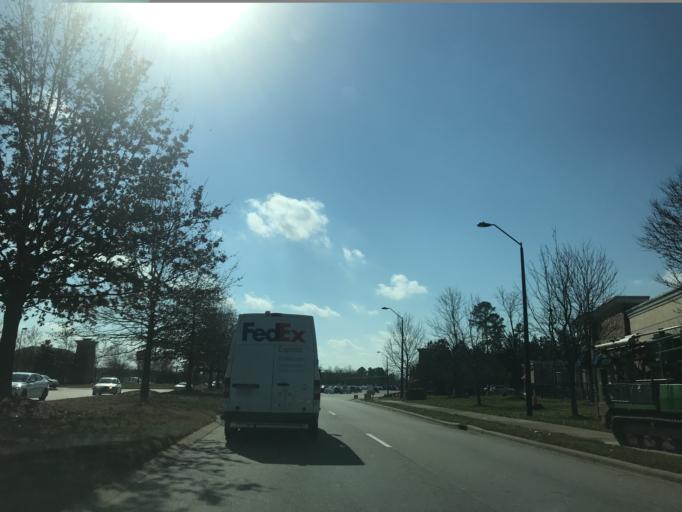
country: US
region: North Carolina
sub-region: Wake County
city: Morrisville
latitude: 35.9142
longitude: -78.7807
